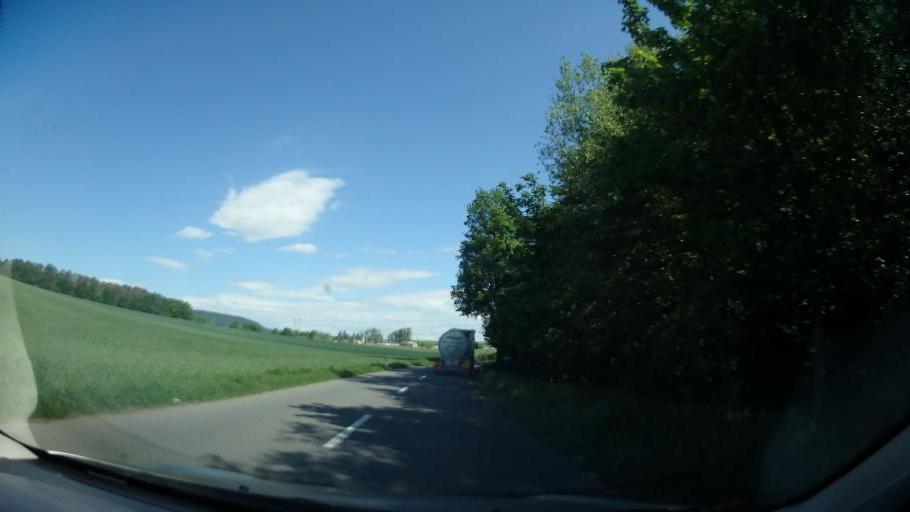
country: CZ
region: Pardubicky
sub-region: Okres Svitavy
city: Moravska Trebova
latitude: 49.6905
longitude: 16.6315
